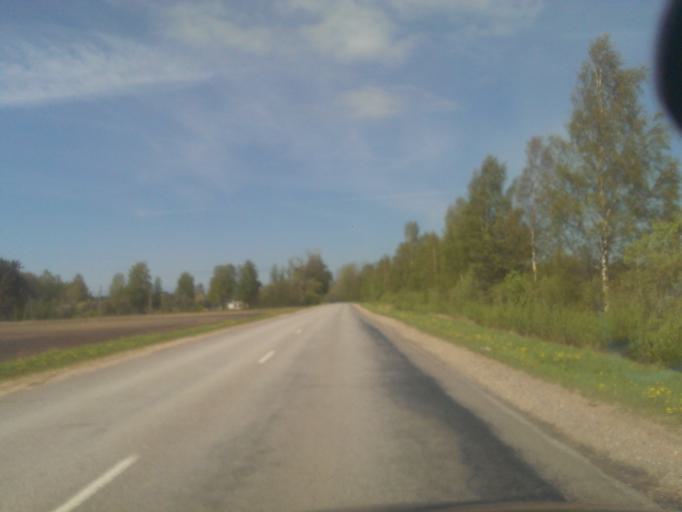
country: LV
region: Ventspils Rajons
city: Piltene
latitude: 57.2777
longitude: 21.5779
